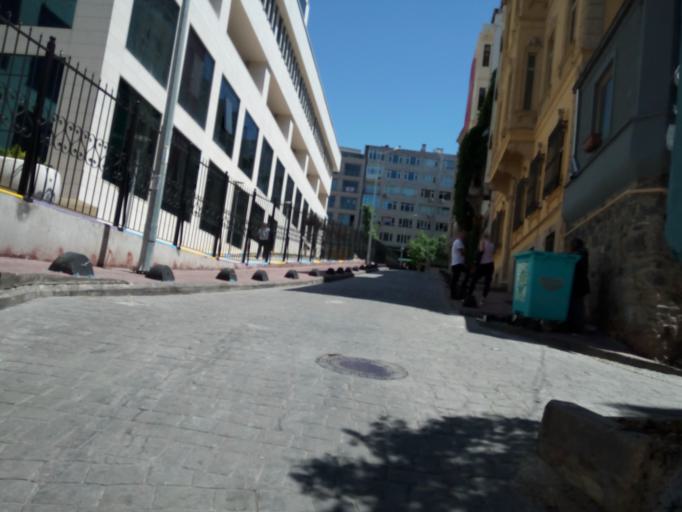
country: TR
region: Istanbul
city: Eminoenue
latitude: 41.0330
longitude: 28.9826
